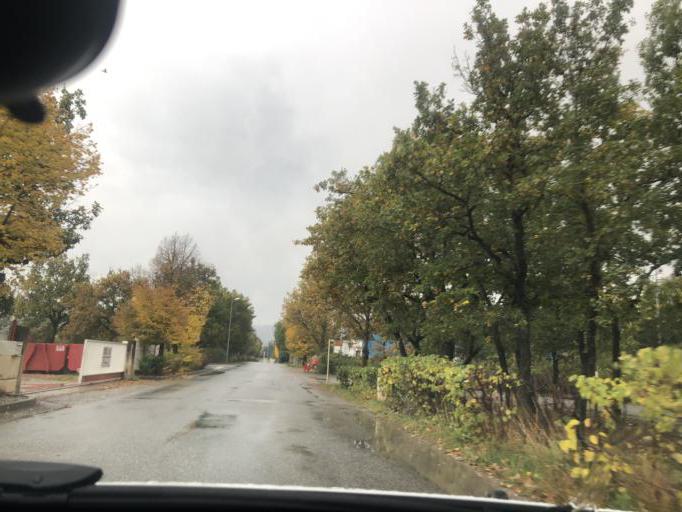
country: FR
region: Provence-Alpes-Cote d'Azur
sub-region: Departement des Alpes-de-Haute-Provence
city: Sisteron
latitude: 44.2284
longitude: 5.9127
